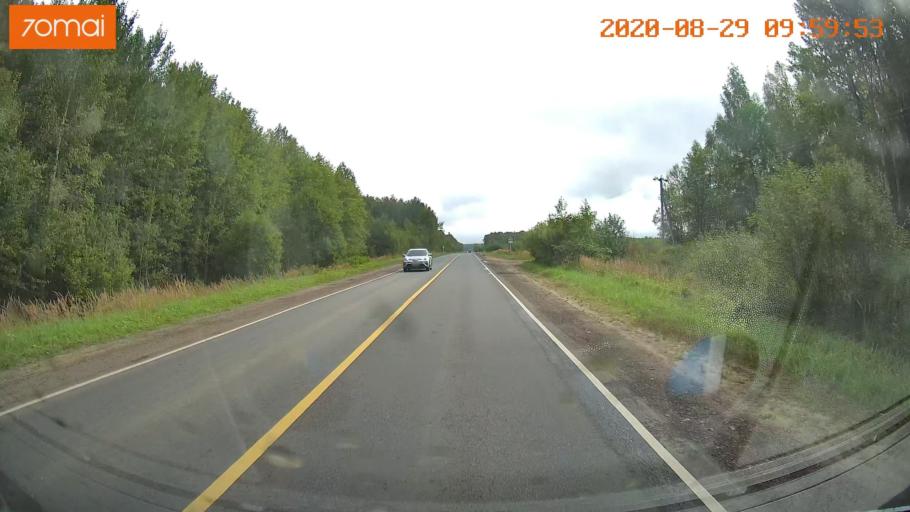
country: RU
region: Ivanovo
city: Zarechnyy
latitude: 57.4104
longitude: 42.3782
